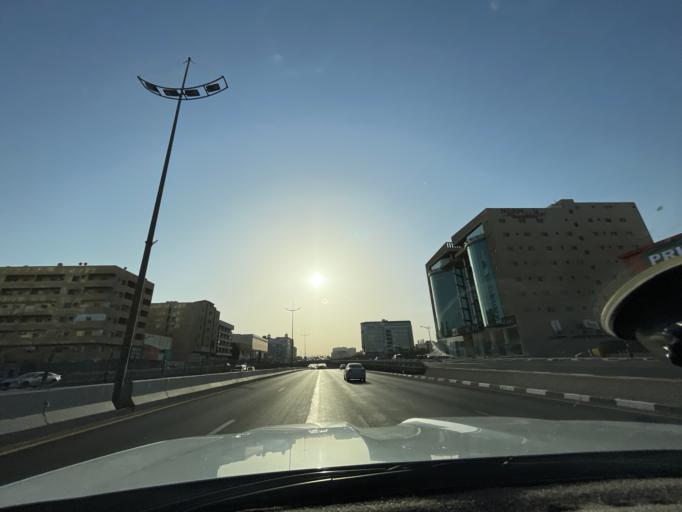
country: SA
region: Eastern Province
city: Khobar
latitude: 26.2852
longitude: 50.1935
